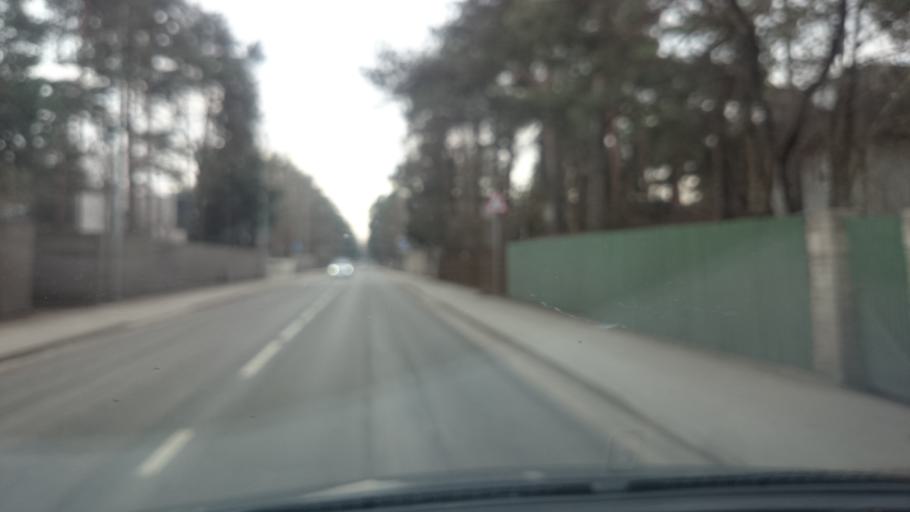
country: EE
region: Harju
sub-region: Saue vald
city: Laagri
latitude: 59.3783
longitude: 24.6360
